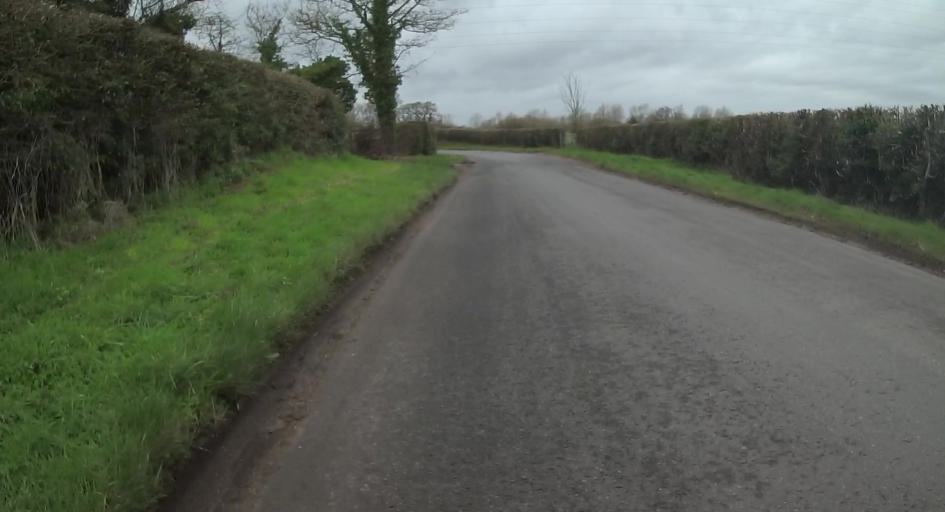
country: GB
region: England
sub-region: Hampshire
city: Kingsclere
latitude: 51.3272
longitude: -1.2607
